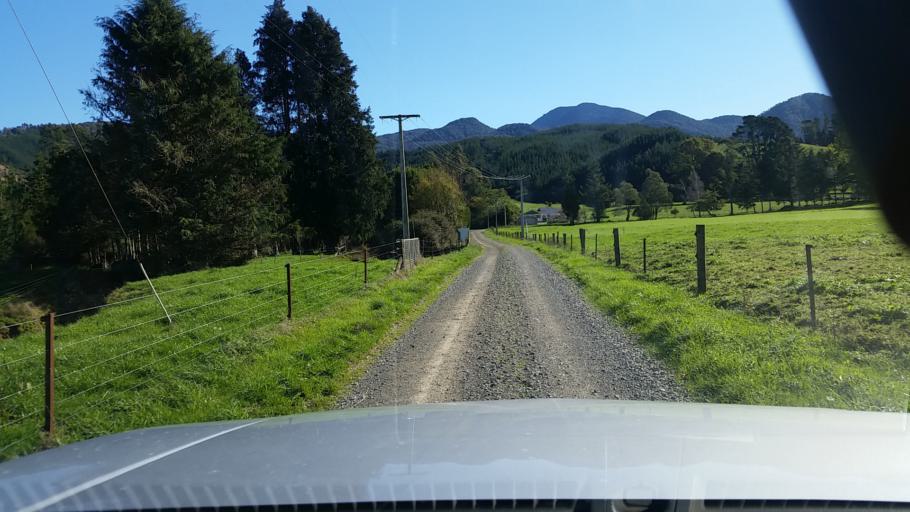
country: NZ
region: Nelson
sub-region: Nelson City
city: Nelson
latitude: -41.2381
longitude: 173.5754
